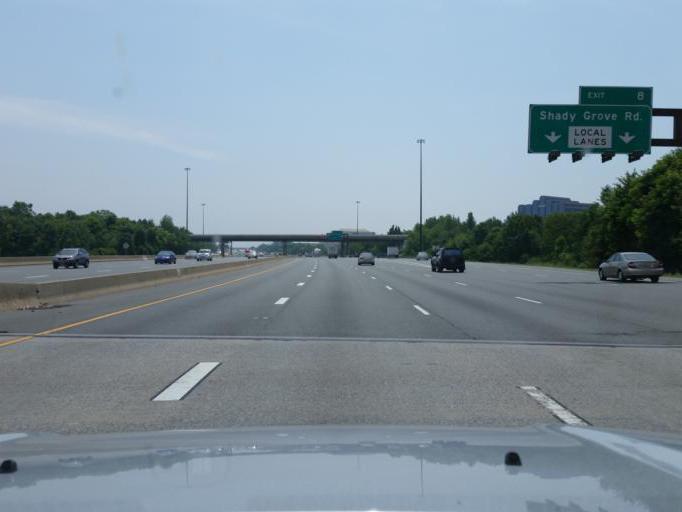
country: US
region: Maryland
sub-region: Montgomery County
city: Gaithersburg
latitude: 39.1212
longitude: -77.1983
